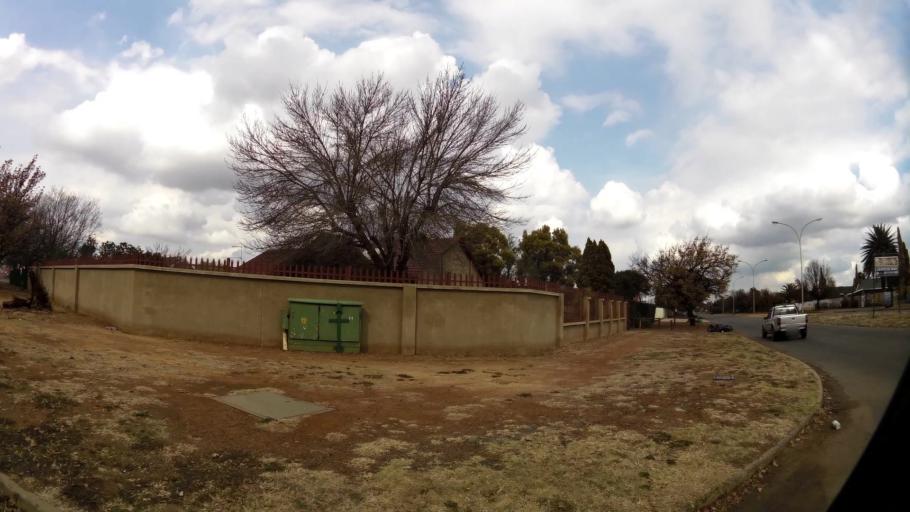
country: ZA
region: Gauteng
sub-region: Sedibeng District Municipality
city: Vanderbijlpark
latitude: -26.7247
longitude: 27.8529
